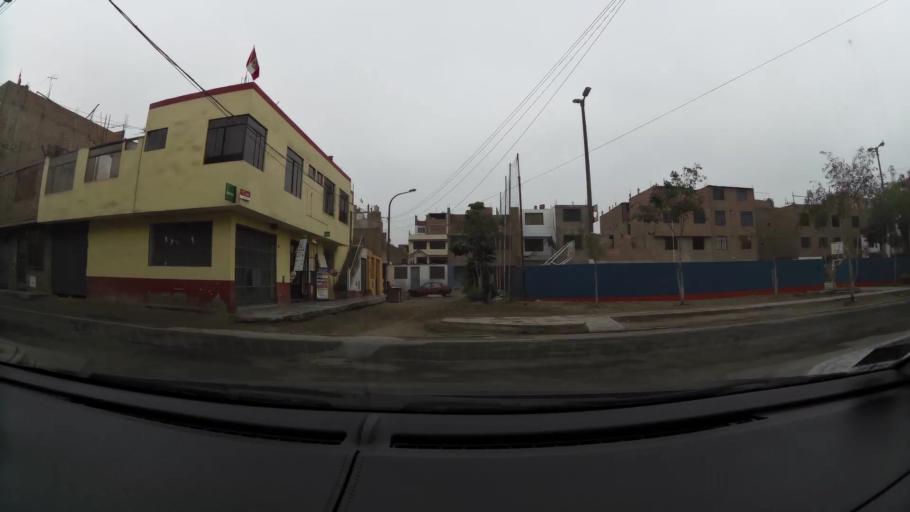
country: PE
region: Lima
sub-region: Lima
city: Independencia
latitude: -11.9753
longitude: -77.0737
